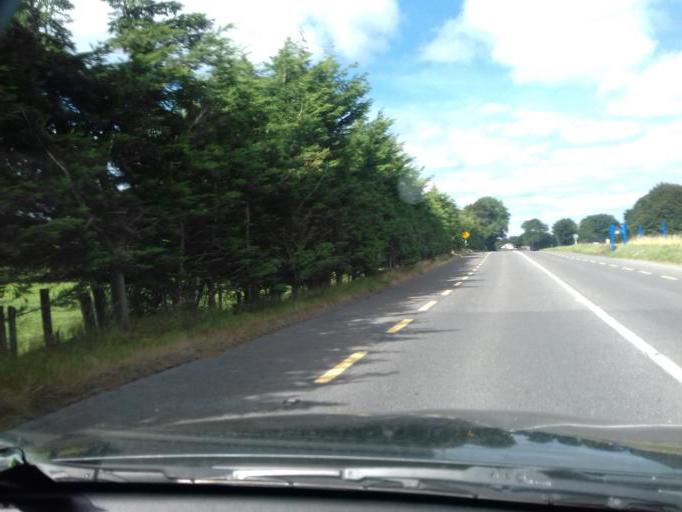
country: IE
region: Leinster
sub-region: Wicklow
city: Valleymount
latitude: 53.1283
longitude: -6.5770
